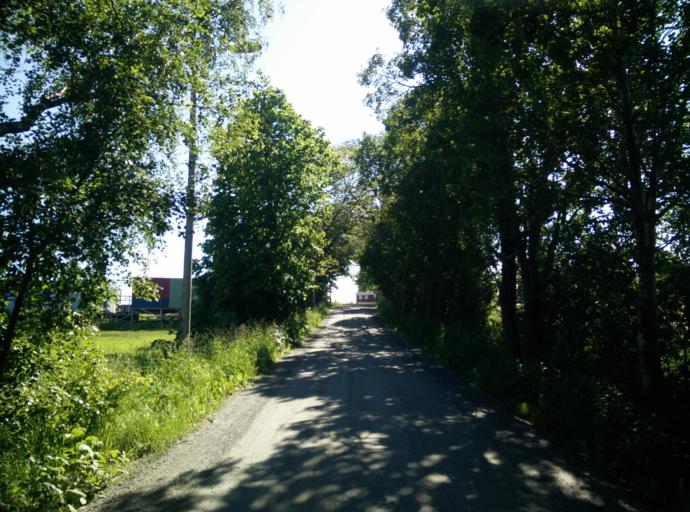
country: NO
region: Sor-Trondelag
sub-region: Trondheim
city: Trondheim
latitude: 63.4077
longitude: 10.3723
